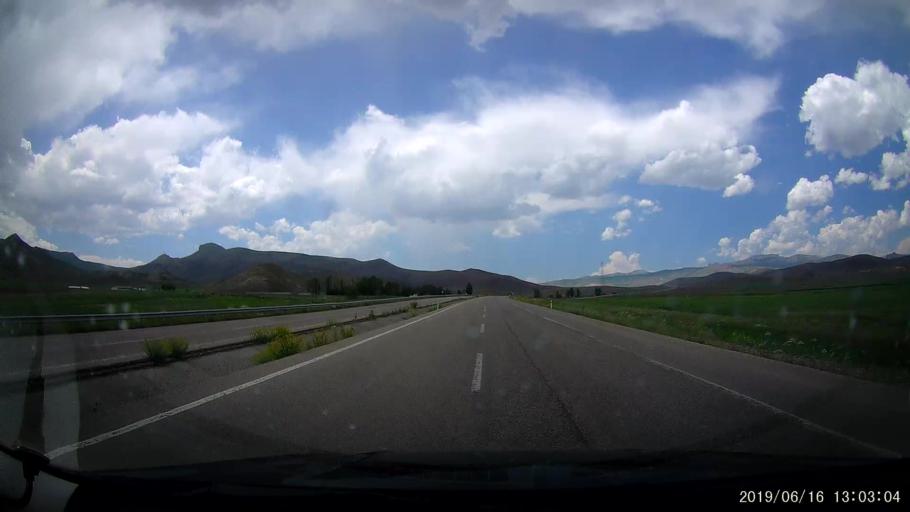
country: TR
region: Agri
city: Sulucem
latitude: 39.5784
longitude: 43.7992
